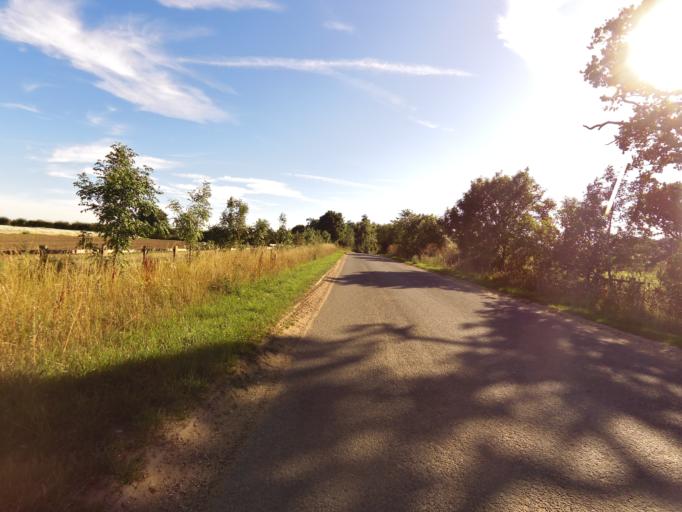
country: GB
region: England
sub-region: Suffolk
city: Kesgrave
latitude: 52.0276
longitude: 1.2580
